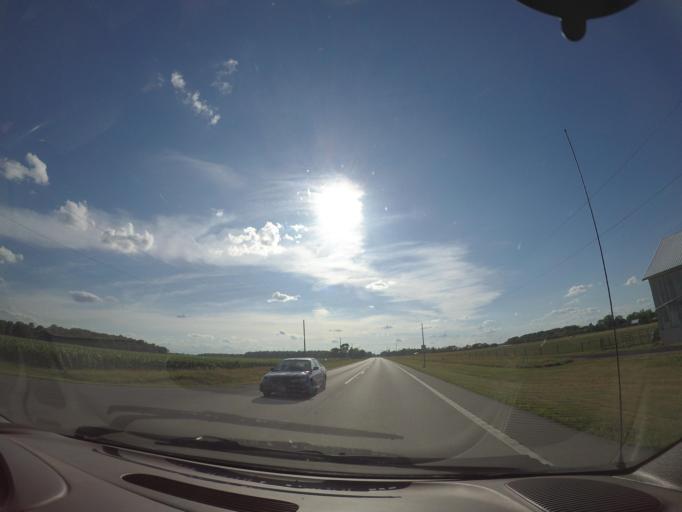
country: US
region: Ohio
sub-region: Henry County
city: Napoleon
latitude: 41.4300
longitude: -84.2085
